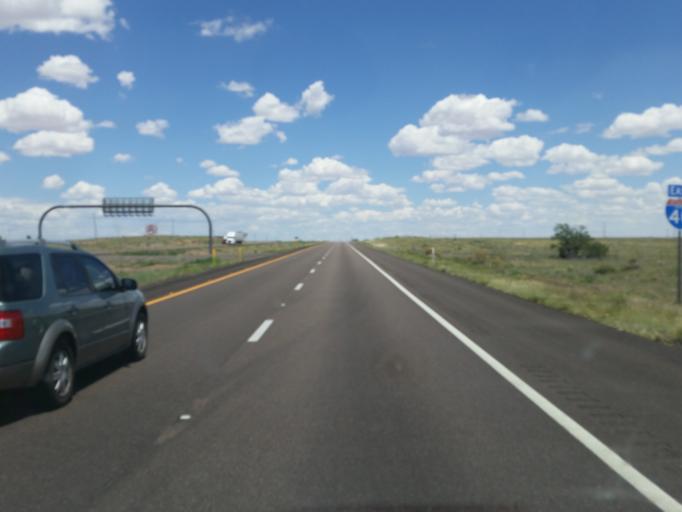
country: US
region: Arizona
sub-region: Navajo County
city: Holbrook
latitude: 34.9816
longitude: -110.0484
